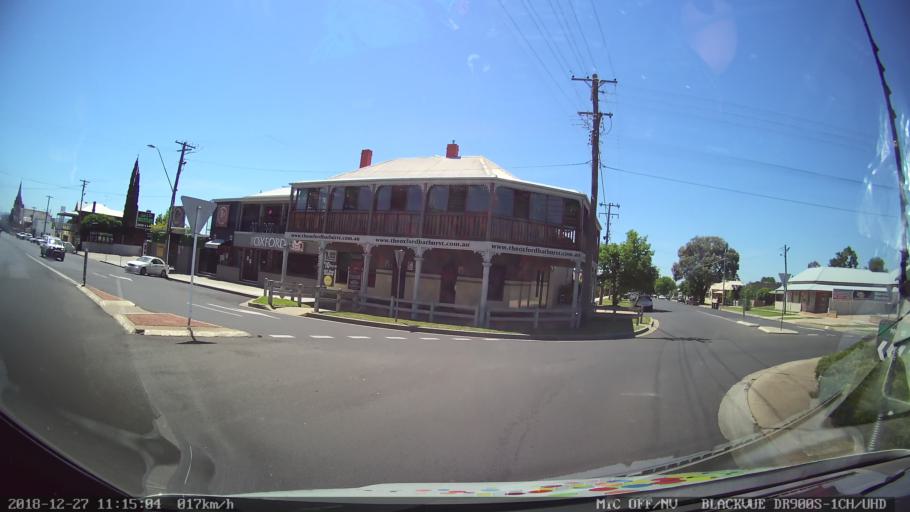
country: AU
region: New South Wales
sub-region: Bathurst Regional
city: Bathurst
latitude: -33.4211
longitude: 149.5755
